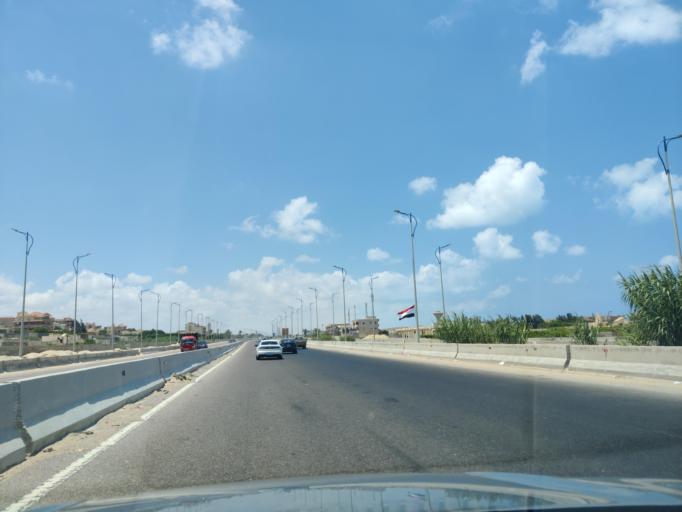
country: EG
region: Alexandria
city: Alexandria
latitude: 30.9769
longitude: 29.5724
